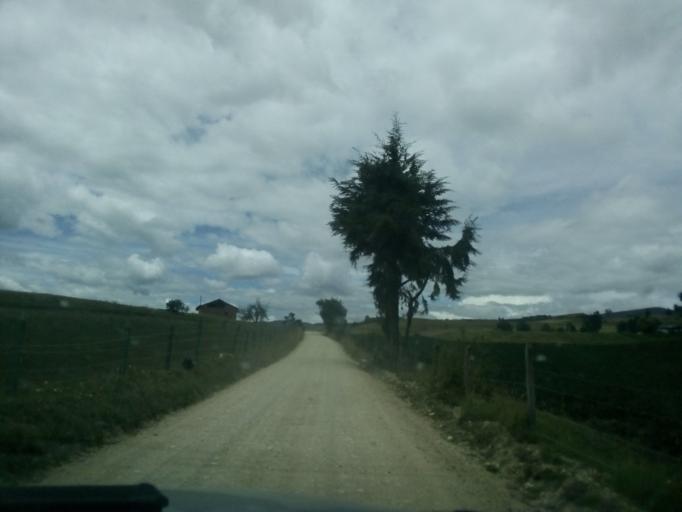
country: CO
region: Boyaca
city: Toca
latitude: 5.5762
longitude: -73.1800
